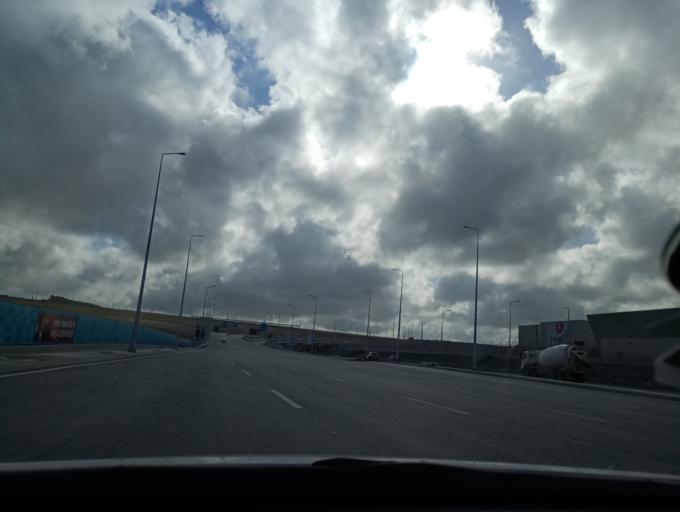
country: TR
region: Istanbul
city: Durusu
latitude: 41.2505
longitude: 28.7390
